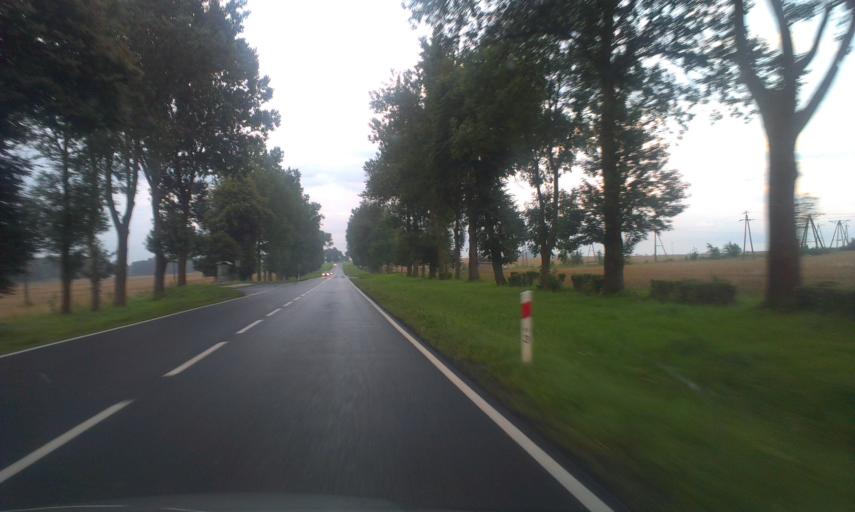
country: PL
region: West Pomeranian Voivodeship
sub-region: Powiat koszalinski
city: Sianow
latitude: 54.1411
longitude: 16.2656
